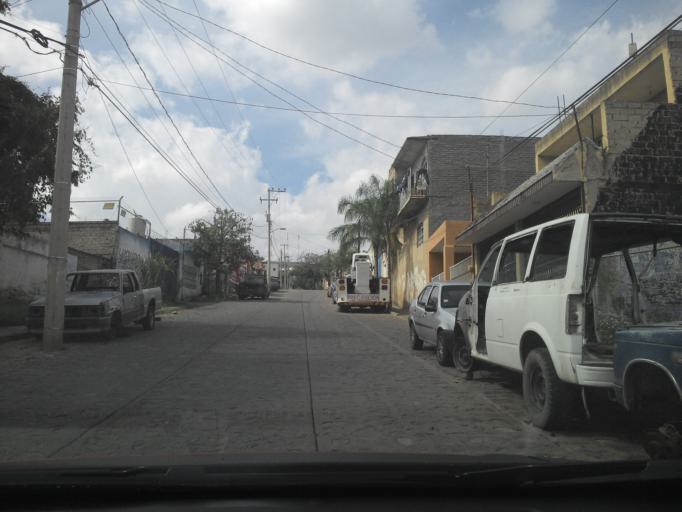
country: MX
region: Jalisco
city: Las Pintas de Arriba
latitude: 20.5937
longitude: -103.3477
